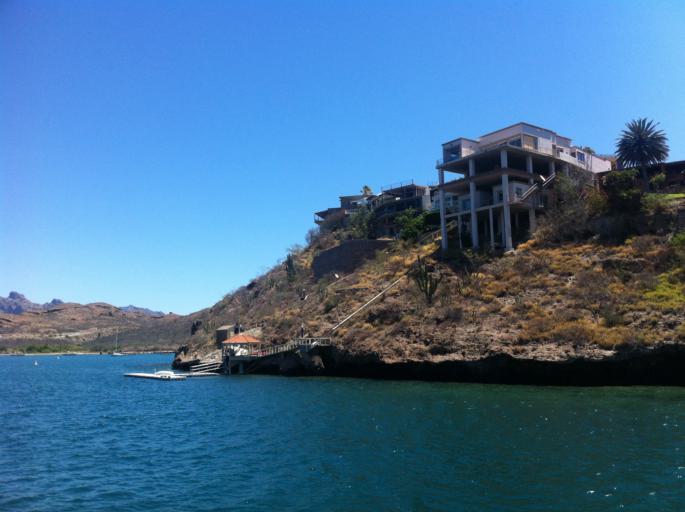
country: MX
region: Sonora
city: Heroica Guaymas
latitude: 27.9439
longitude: -111.0600
